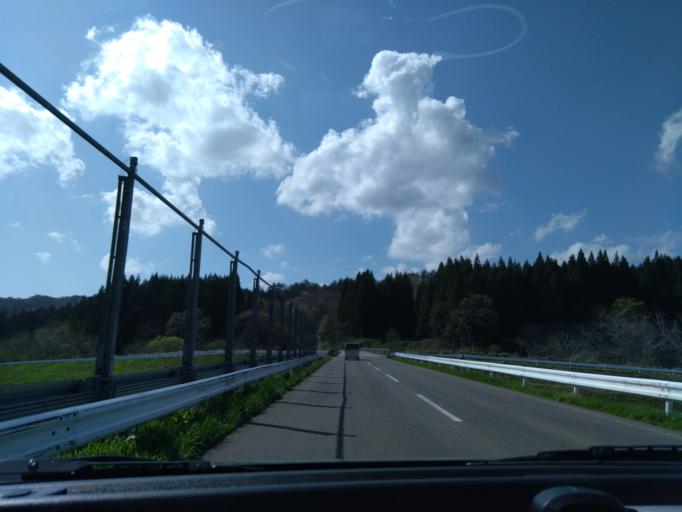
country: JP
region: Akita
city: Akita
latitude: 39.6950
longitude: 140.2700
